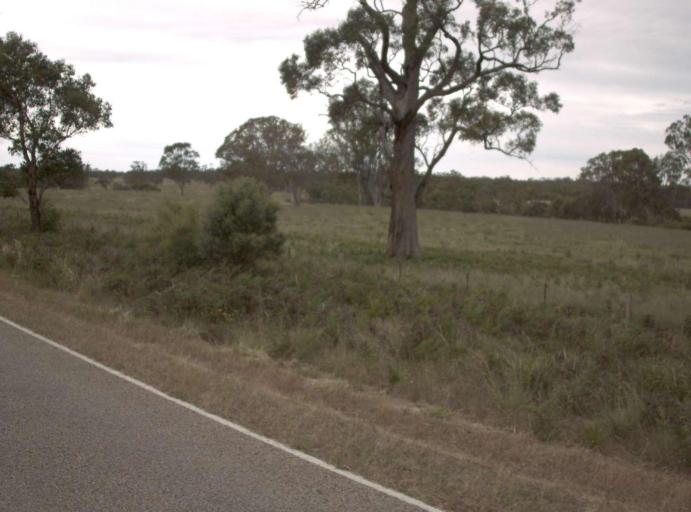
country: AU
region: Victoria
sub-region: Wellington
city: Sale
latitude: -38.0058
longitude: 147.2788
